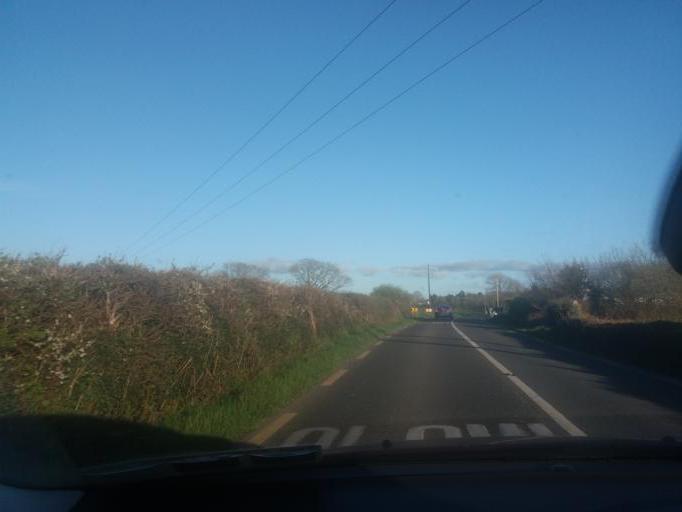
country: IE
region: Munster
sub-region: Ciarrai
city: Killorglin
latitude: 52.1370
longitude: -9.7007
